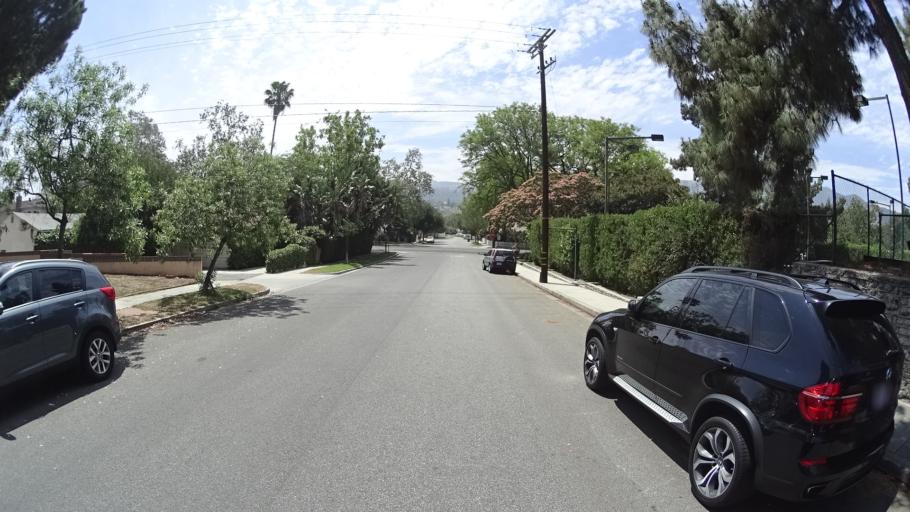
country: US
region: California
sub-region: Los Angeles County
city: Burbank
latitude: 34.1583
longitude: -118.3151
